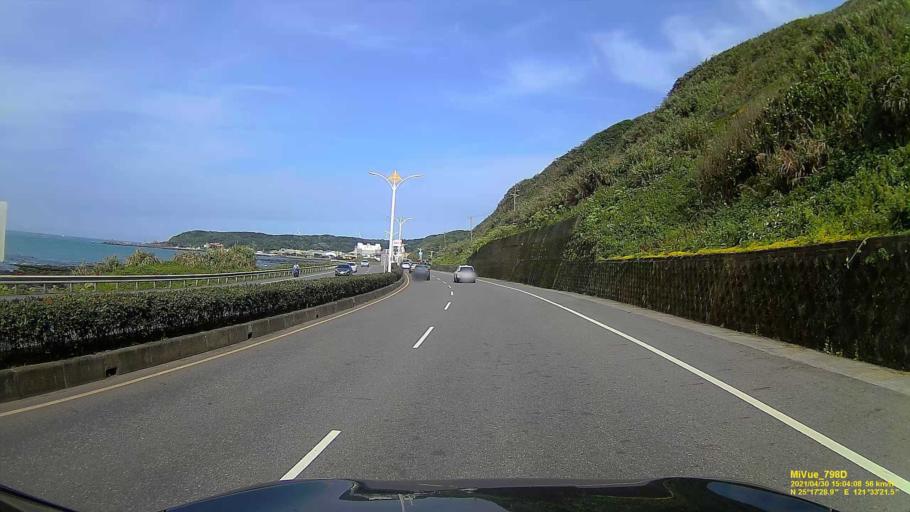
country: TW
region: Taipei
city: Taipei
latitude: 25.2913
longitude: 121.5561
